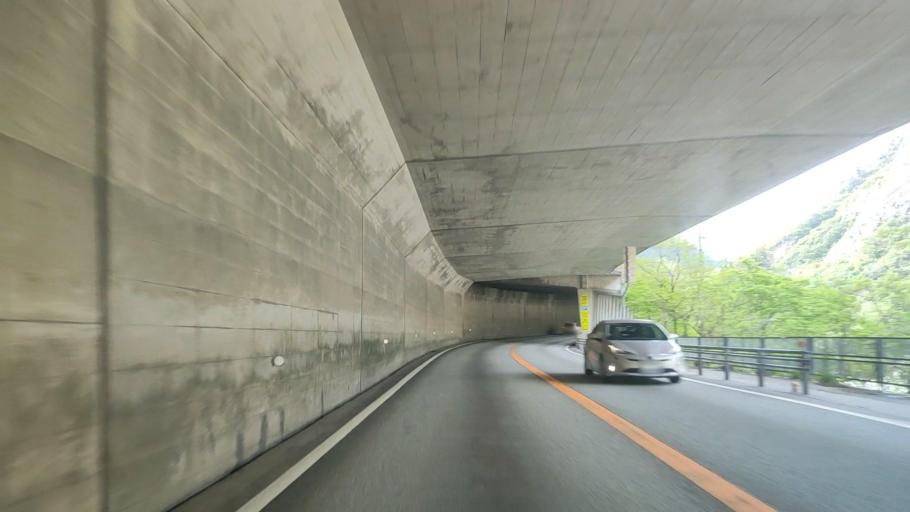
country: JP
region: Gifu
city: Takayama
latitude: 36.3479
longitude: 137.2930
